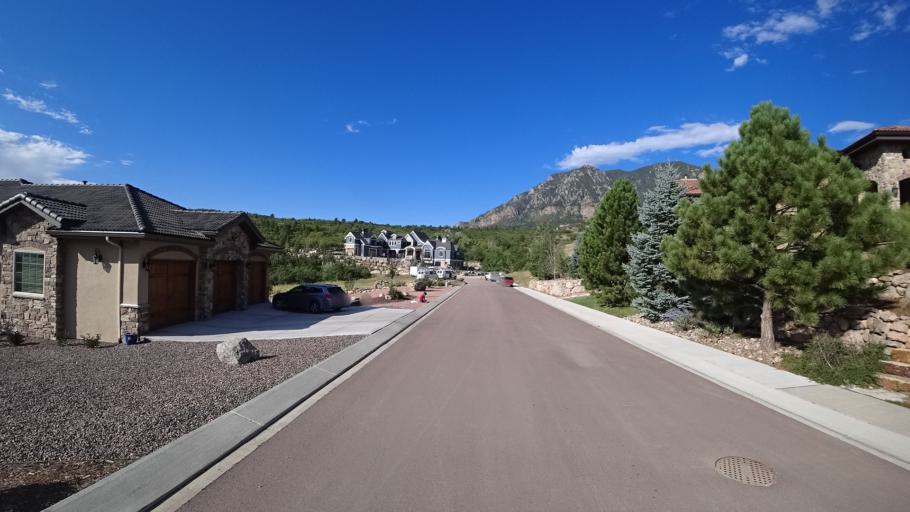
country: US
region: Colorado
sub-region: El Paso County
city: Fort Carson
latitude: 38.7535
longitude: -104.8212
